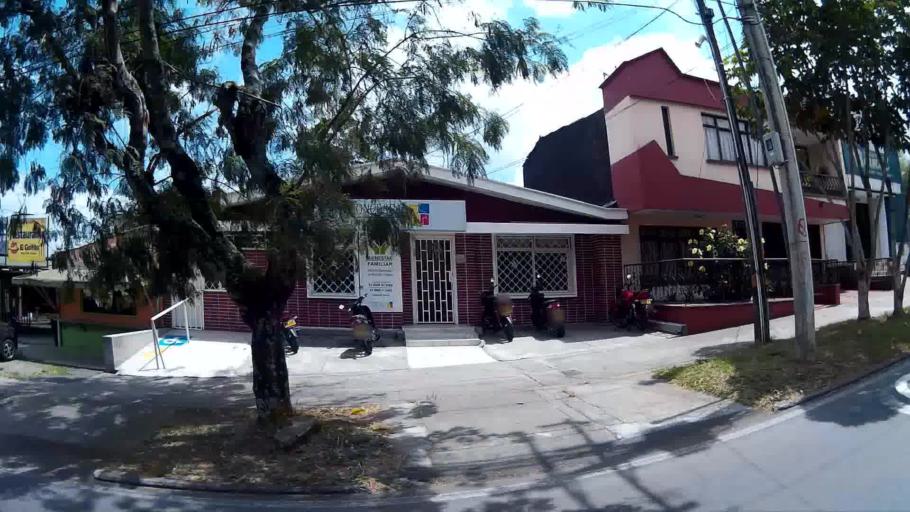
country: CO
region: Quindio
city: Calarca
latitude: 4.5656
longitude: -75.6495
